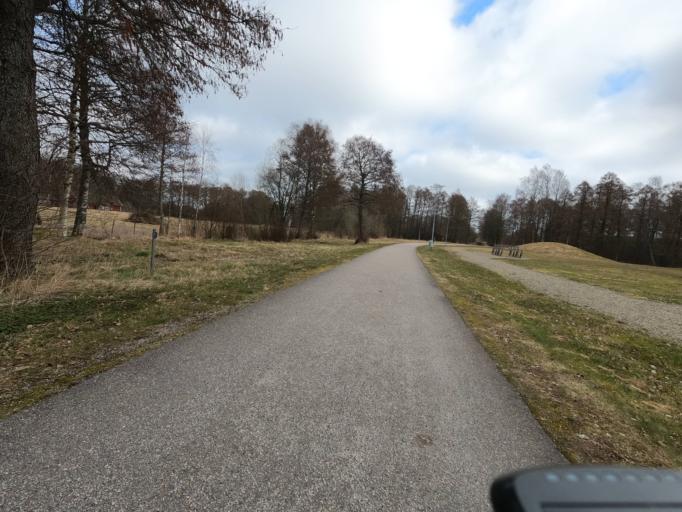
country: SE
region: Joenkoeping
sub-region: Varnamo Kommun
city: Rydaholm
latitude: 56.8630
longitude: 14.1662
